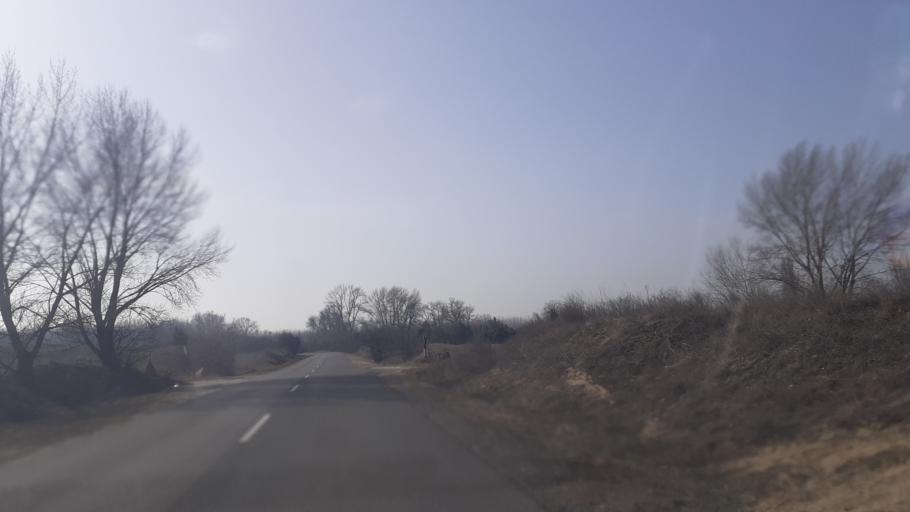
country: HU
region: Pest
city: Orkeny
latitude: 47.0993
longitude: 19.3892
